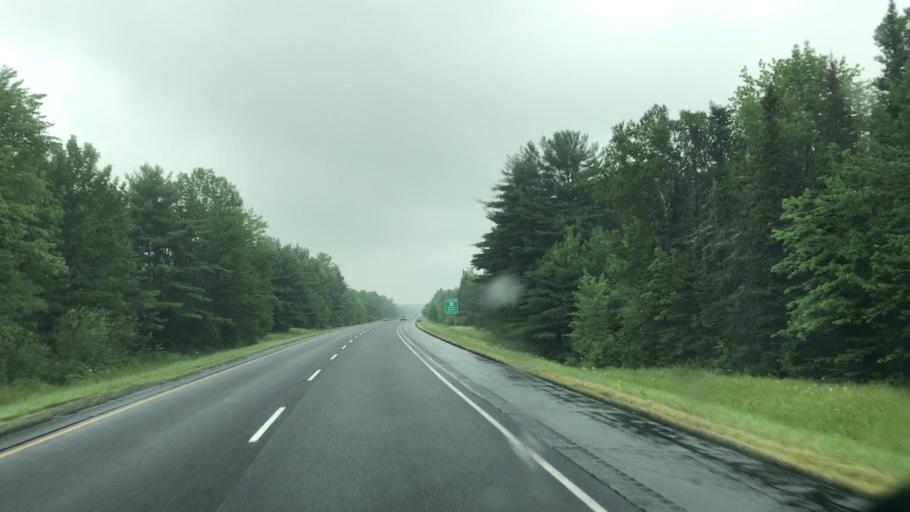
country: US
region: Maine
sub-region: Penobscot County
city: Orono
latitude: 44.9306
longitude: -68.7057
